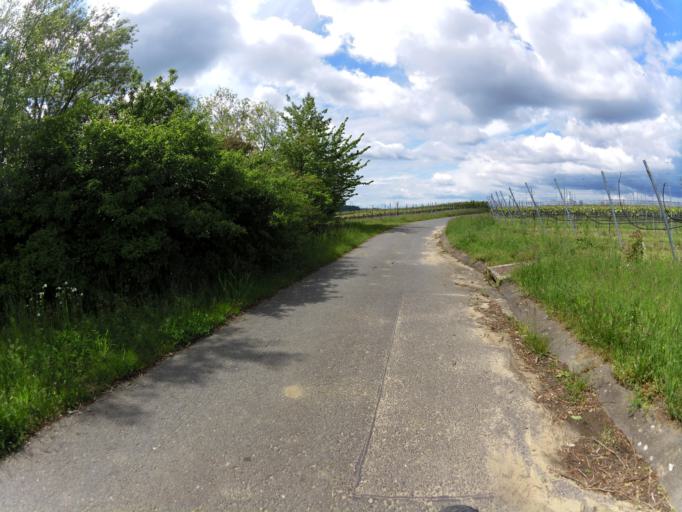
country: DE
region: Bavaria
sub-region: Regierungsbezirk Unterfranken
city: Nordheim
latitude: 49.8439
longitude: 10.1878
